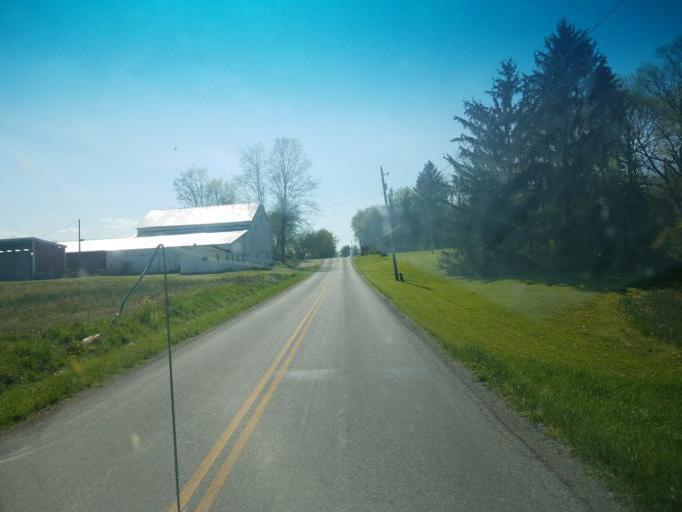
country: US
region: Ohio
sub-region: Medina County
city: Westfield Center
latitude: 40.9858
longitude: -81.9395
